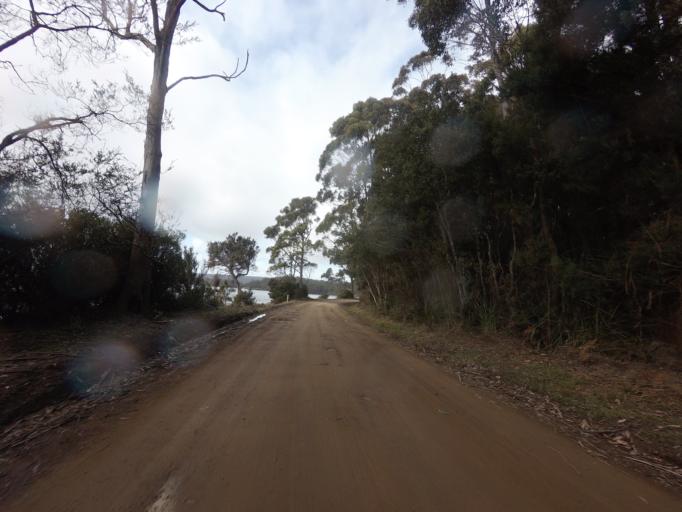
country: AU
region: Tasmania
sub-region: Huon Valley
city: Geeveston
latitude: -43.5461
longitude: 146.8893
